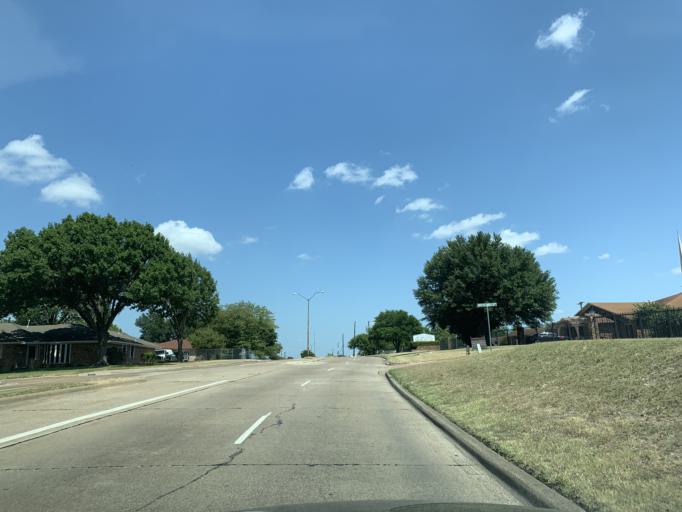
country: US
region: Texas
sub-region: Dallas County
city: DeSoto
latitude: 32.6750
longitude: -96.8096
